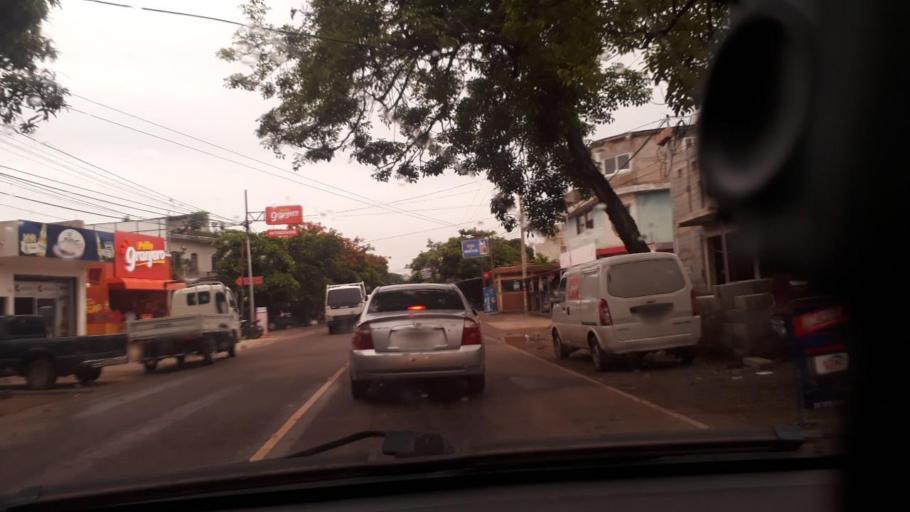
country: GT
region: Jutiapa
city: Asuncion Mita
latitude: 14.3370
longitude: -89.7132
